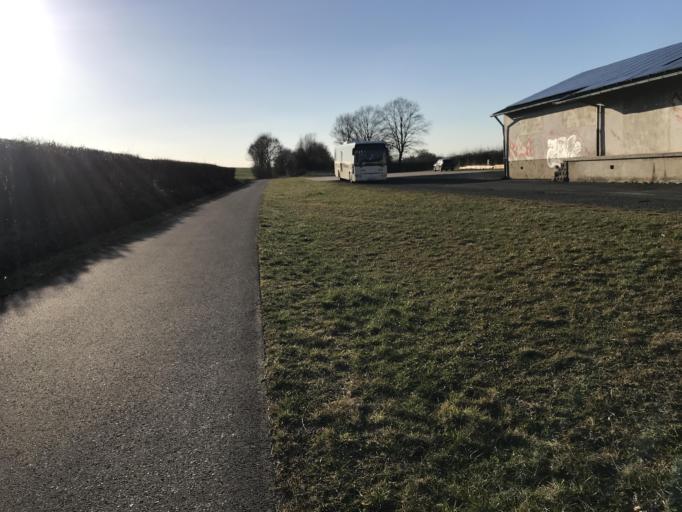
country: DE
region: Hesse
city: Neukirchen
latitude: 50.8742
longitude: 9.3085
